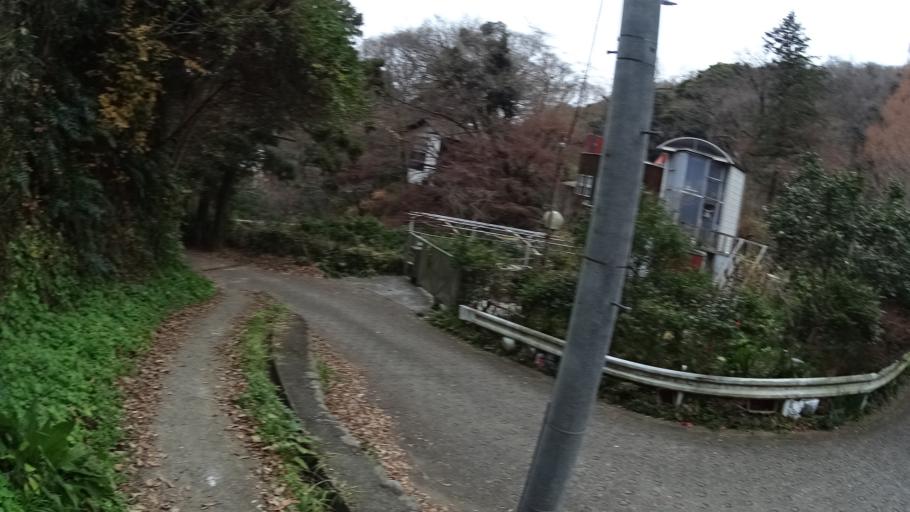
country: JP
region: Kanagawa
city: Oiso
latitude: 35.3171
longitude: 139.3084
